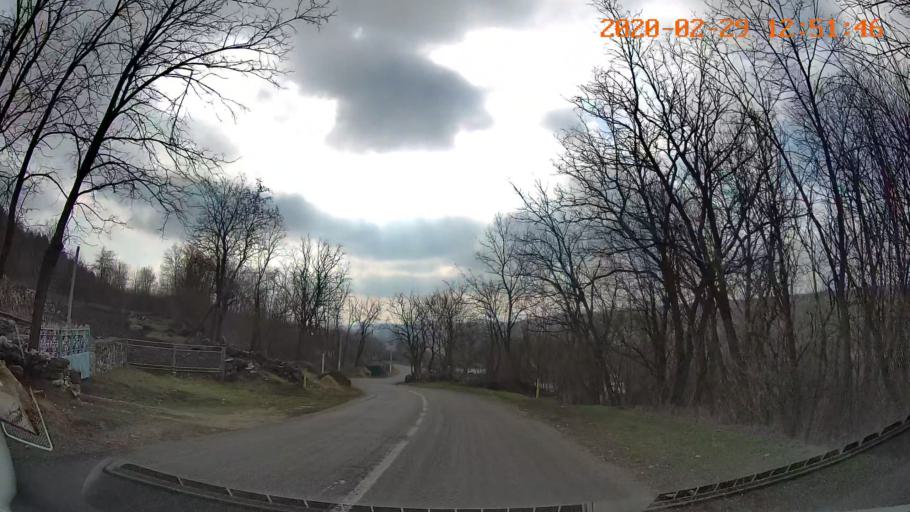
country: MD
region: Telenesti
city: Camenca
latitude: 48.1171
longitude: 28.7324
